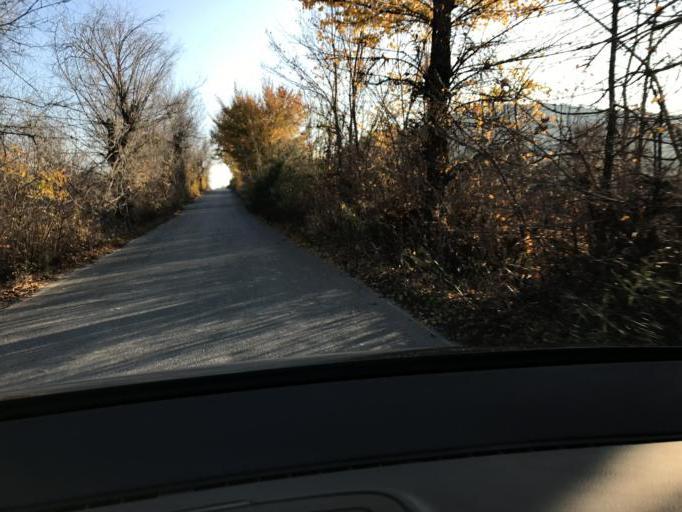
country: ES
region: Andalusia
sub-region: Provincia de Granada
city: Albolote
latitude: 37.2572
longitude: -3.6751
